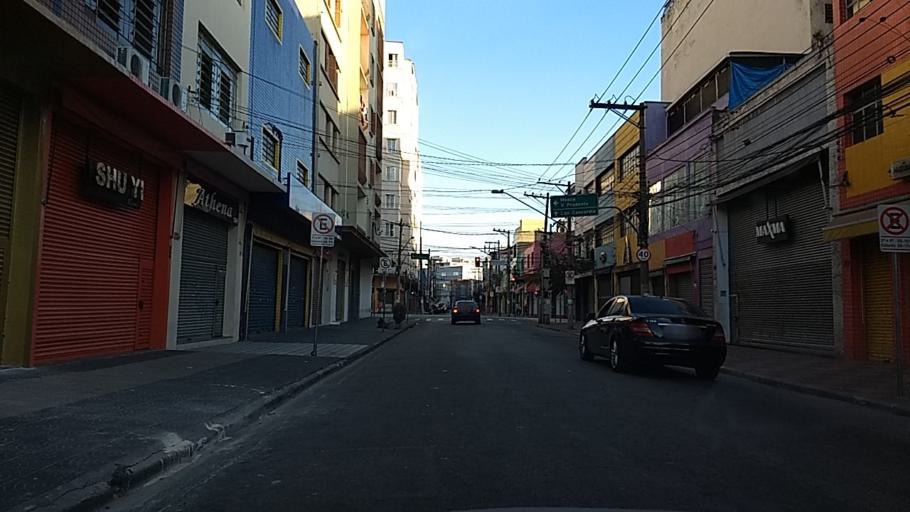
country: BR
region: Sao Paulo
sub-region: Sao Paulo
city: Sao Paulo
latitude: -23.5373
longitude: -46.6190
